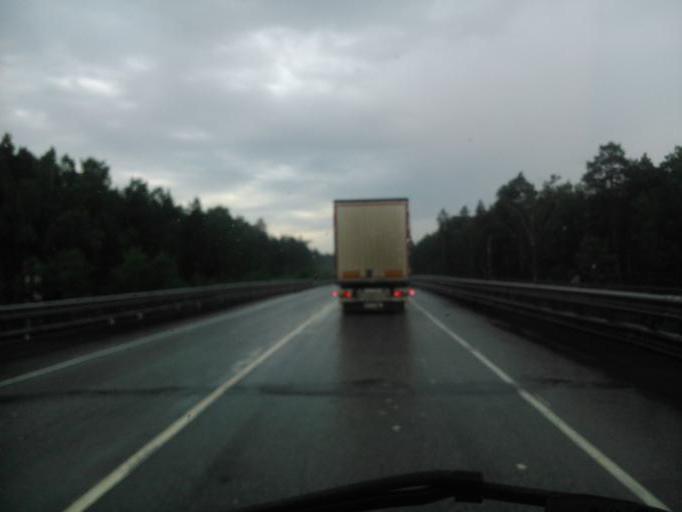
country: RU
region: Sverdlovsk
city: Istok
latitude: 56.8390
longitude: 60.8014
